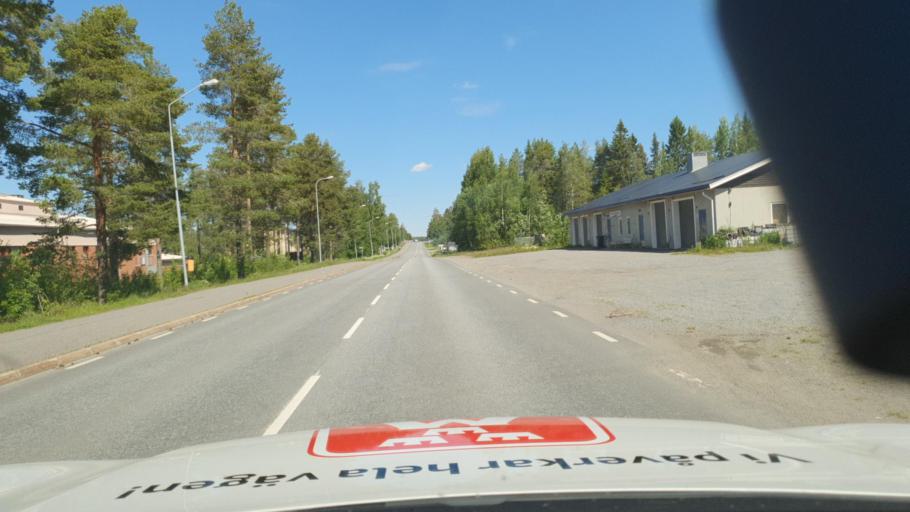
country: SE
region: Vaesterbotten
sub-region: Skelleftea Kommun
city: Boliden
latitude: 64.8608
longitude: 20.3852
